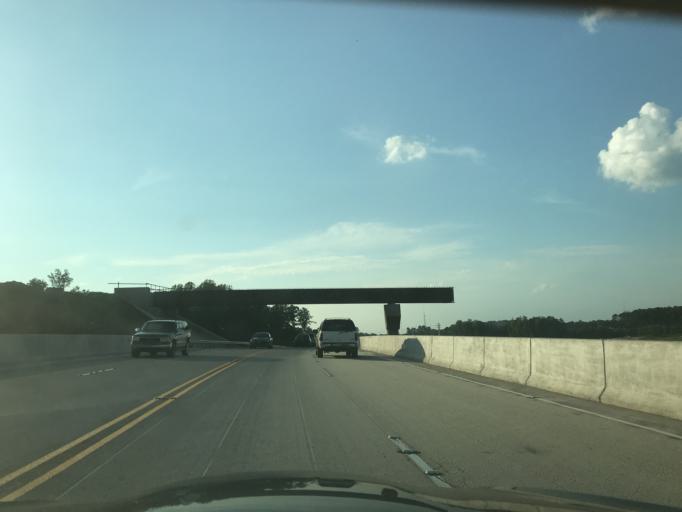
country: US
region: North Carolina
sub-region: Durham County
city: Durham
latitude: 35.9753
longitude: -78.8547
